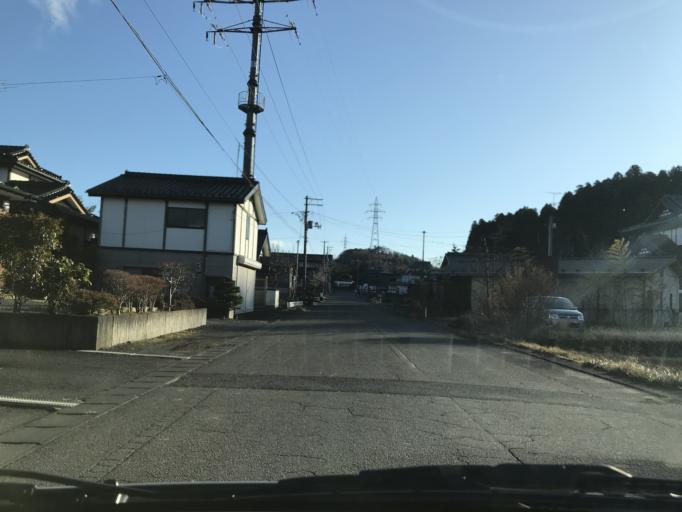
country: JP
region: Iwate
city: Ichinoseki
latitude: 39.0017
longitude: 141.1079
